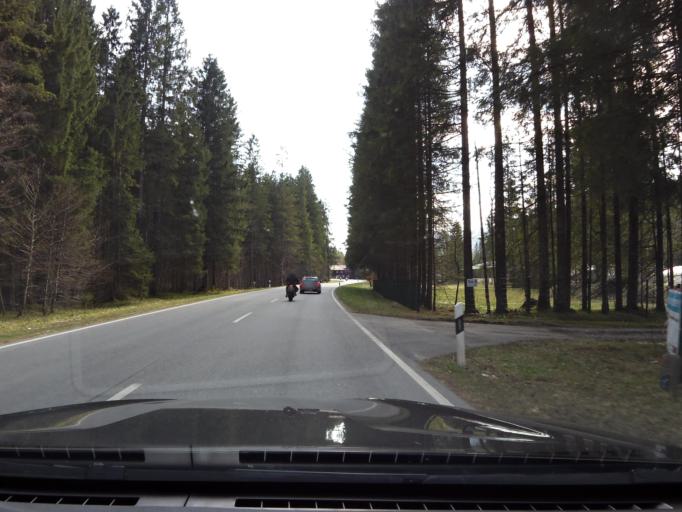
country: DE
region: Bavaria
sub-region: Upper Bavaria
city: Wallgau
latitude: 47.5571
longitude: 11.2926
